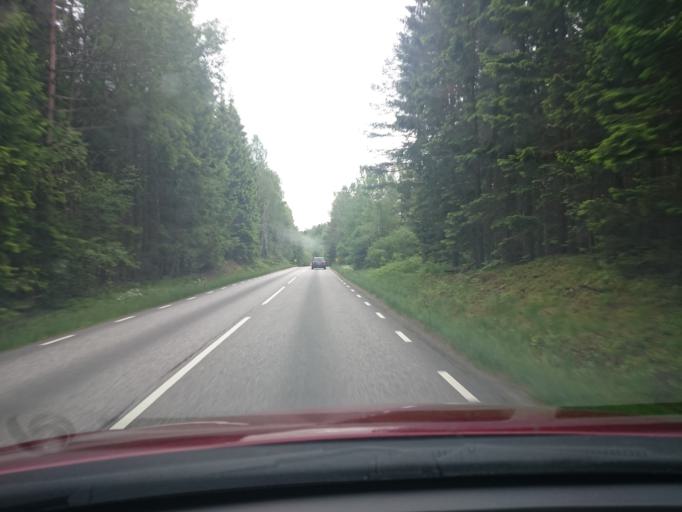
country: SE
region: Vaestra Goetaland
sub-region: Lerums Kommun
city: Stenkullen
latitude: 57.7626
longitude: 12.3084
